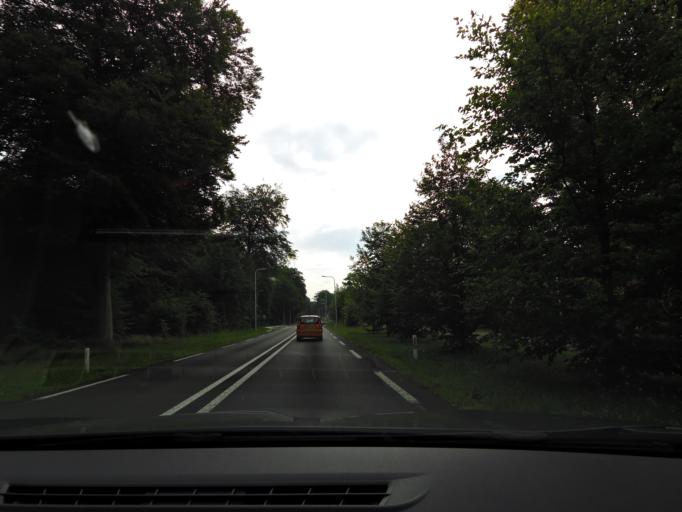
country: NL
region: Gelderland
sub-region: Gemeente Renkum
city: Doorwerth
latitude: 51.9864
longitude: 5.7903
